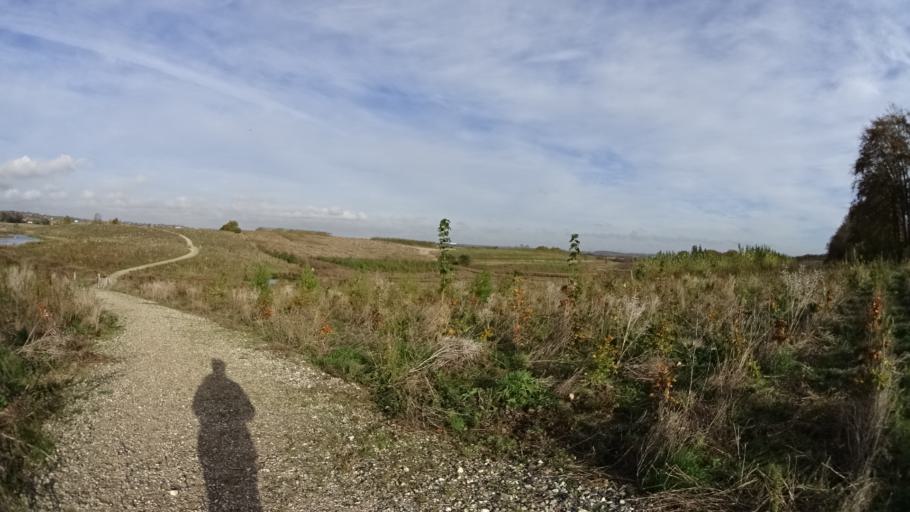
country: DK
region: Central Jutland
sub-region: Arhus Kommune
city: Framlev
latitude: 56.1249
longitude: 10.0227
